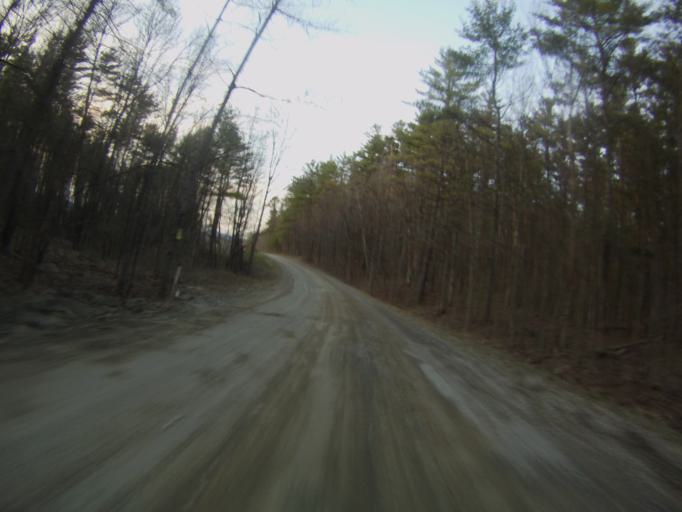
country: US
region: Vermont
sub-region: Addison County
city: Middlebury (village)
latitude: 44.0264
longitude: -73.2207
